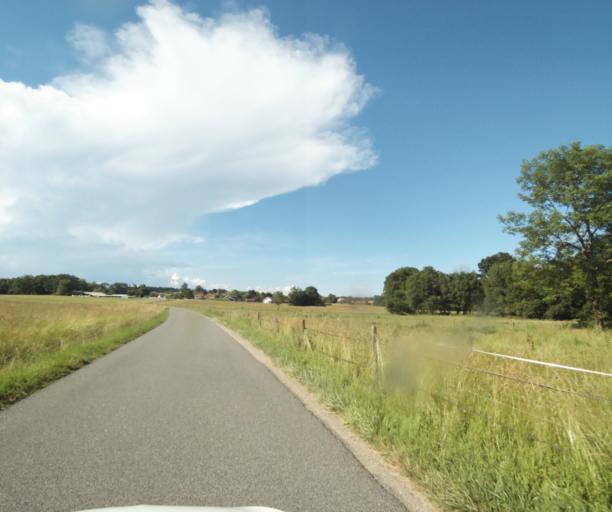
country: FR
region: Rhone-Alpes
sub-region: Departement de la Haute-Savoie
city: Massongy
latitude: 46.3417
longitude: 6.3303
